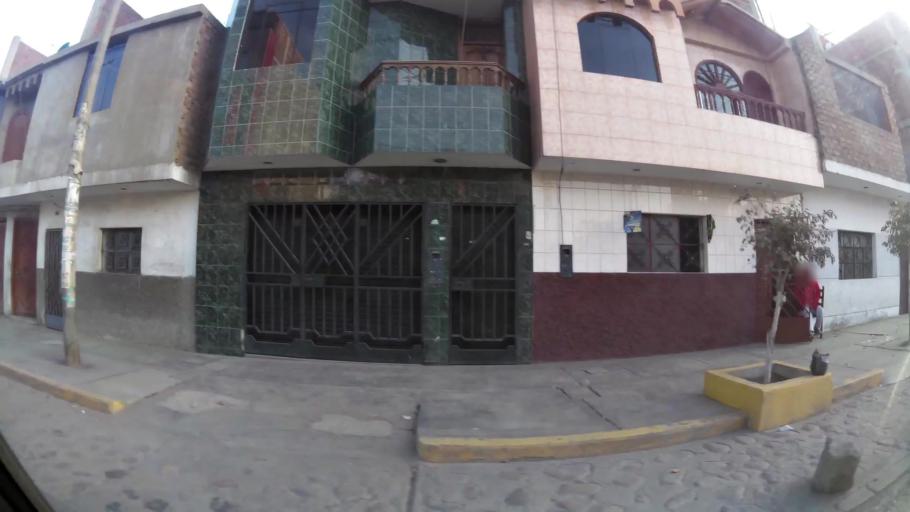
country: PE
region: La Libertad
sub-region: Provincia de Trujillo
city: El Porvenir
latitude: -8.0777
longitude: -78.9972
